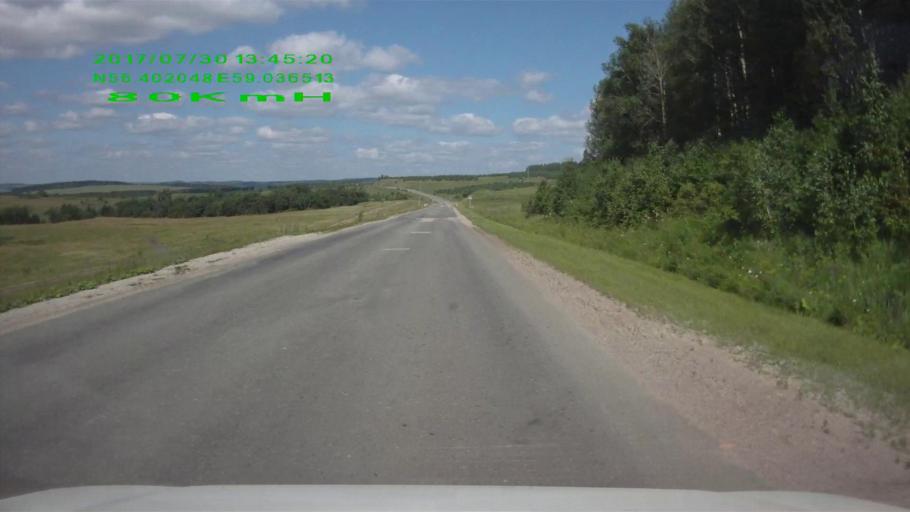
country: RU
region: Sverdlovsk
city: Mikhaylovsk
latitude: 56.4017
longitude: 59.0362
